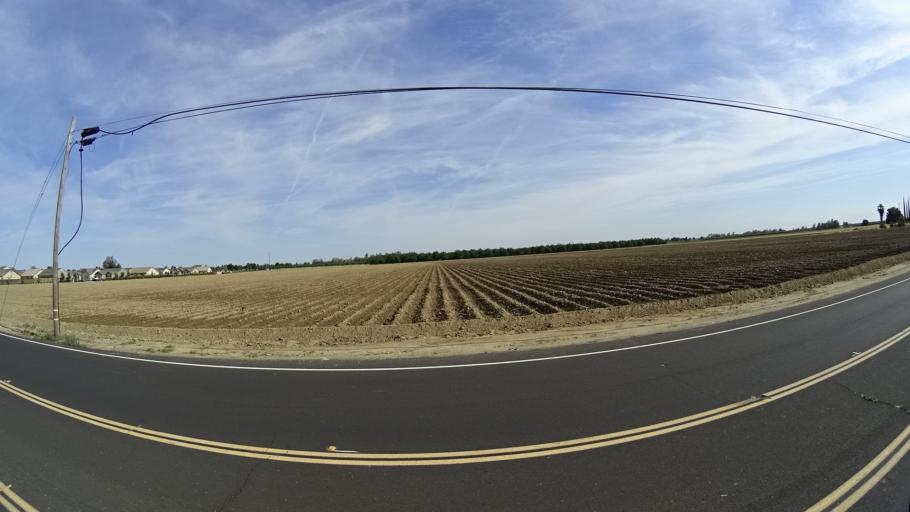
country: US
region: California
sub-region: Kings County
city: Hanford
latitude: 36.3424
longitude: -119.6218
